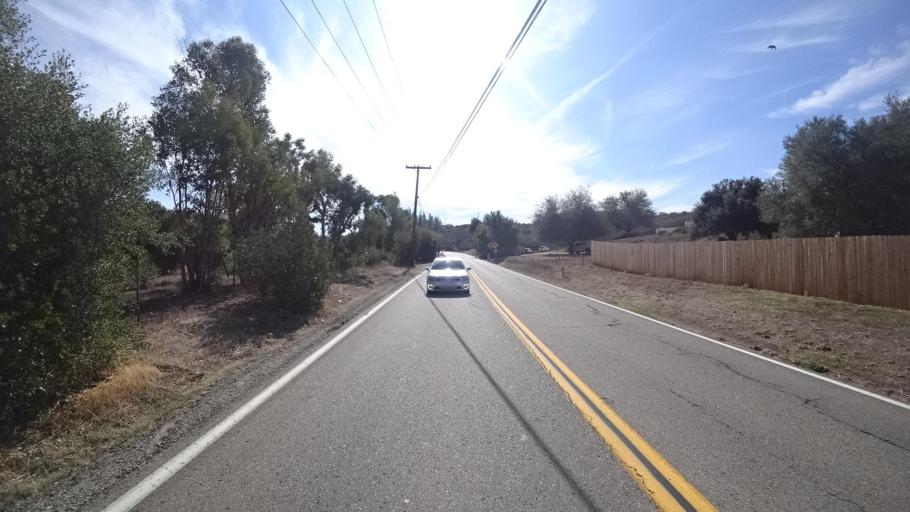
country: US
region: California
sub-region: San Diego County
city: Harbison Canyon
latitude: 32.8383
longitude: -116.8037
